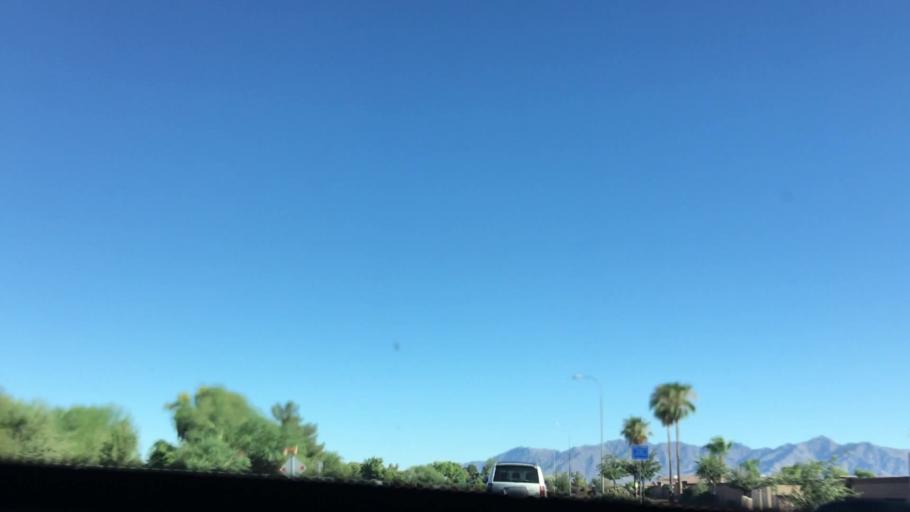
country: US
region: Arizona
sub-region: Maricopa County
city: Laveen
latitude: 33.3909
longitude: -112.2028
